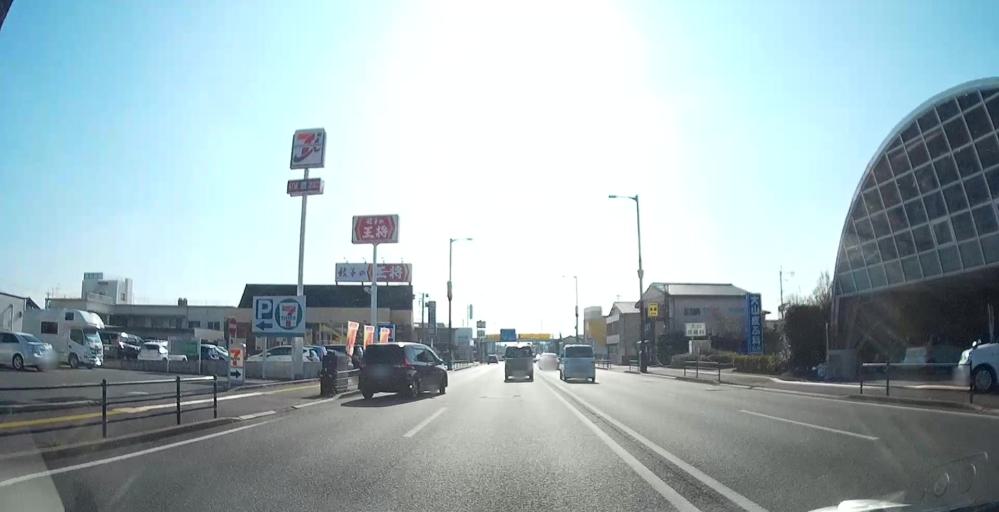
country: JP
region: Kumamoto
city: Kumamoto
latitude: 32.7672
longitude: 130.6918
